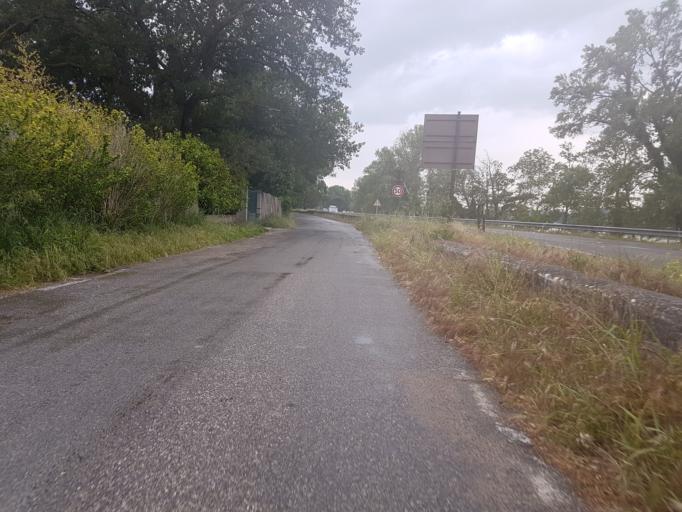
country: FR
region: Provence-Alpes-Cote d'Azur
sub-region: Departement du Vaucluse
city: Avignon
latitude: 43.9632
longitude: 4.8151
